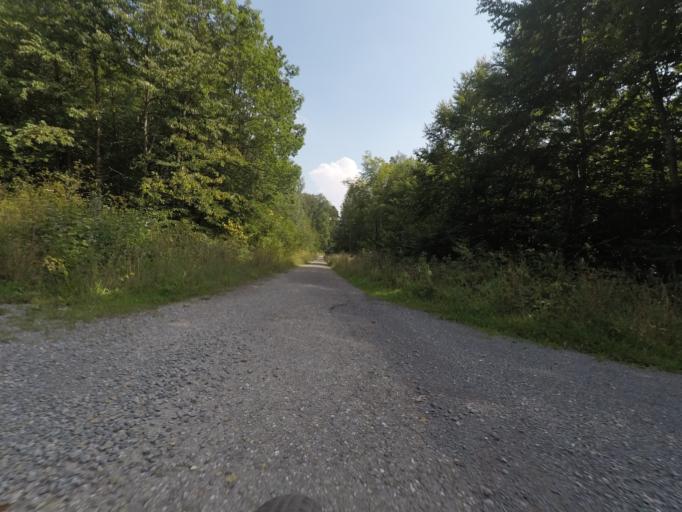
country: DE
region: Baden-Wuerttemberg
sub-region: Regierungsbezirk Stuttgart
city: Steinenbronn
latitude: 48.7072
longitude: 9.0873
